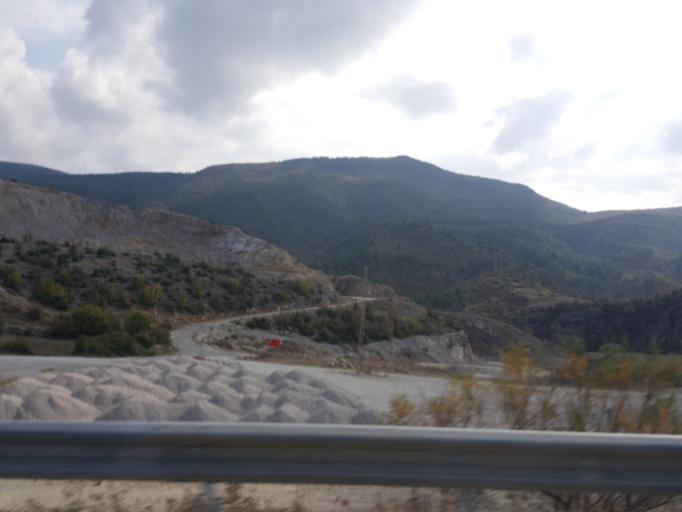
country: TR
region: Sinop
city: Sarayduzu
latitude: 41.3707
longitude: 34.8961
